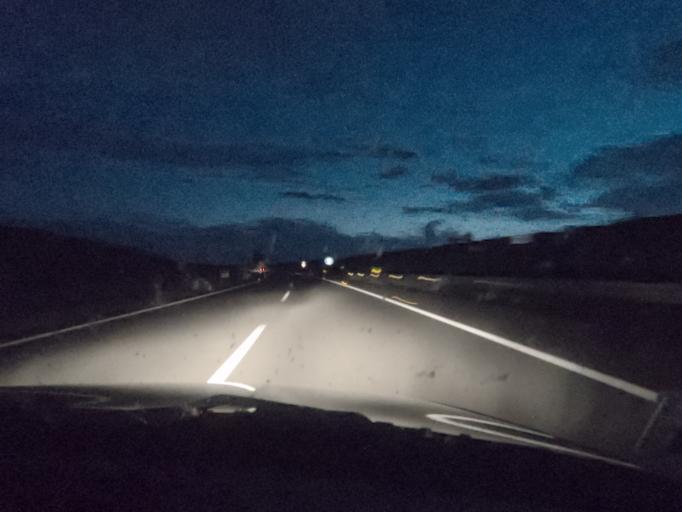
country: ES
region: Extremadura
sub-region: Provincia de Caceres
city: Galisteo
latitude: 39.9814
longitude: -6.3224
